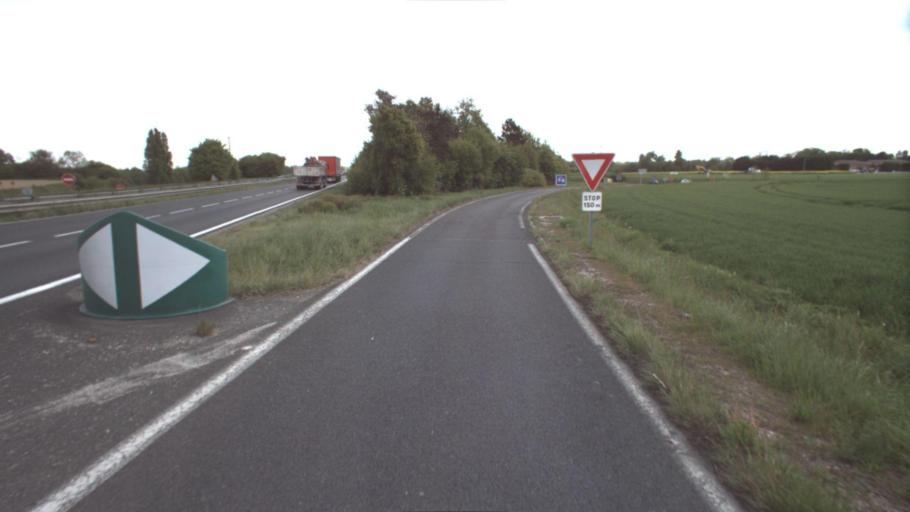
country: FR
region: Ile-de-France
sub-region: Departement de Seine-et-Marne
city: Rozay-en-Brie
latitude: 48.6855
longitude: 2.9343
